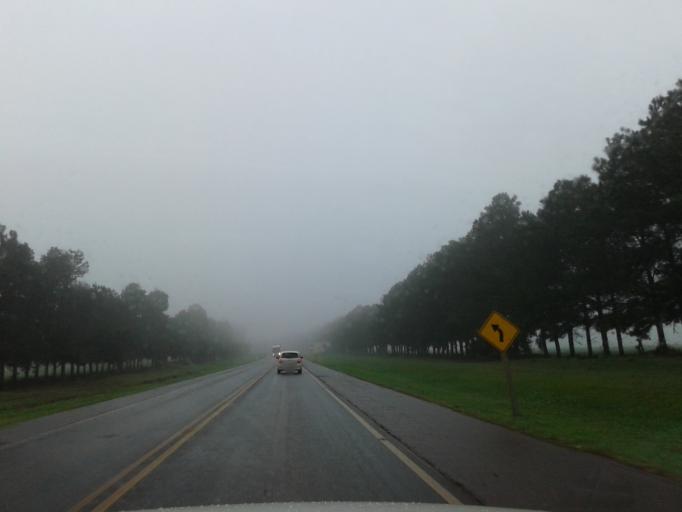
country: PY
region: Itapua
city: Arquitecto Tomas Romero Pereira
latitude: -26.5506
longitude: -55.2625
